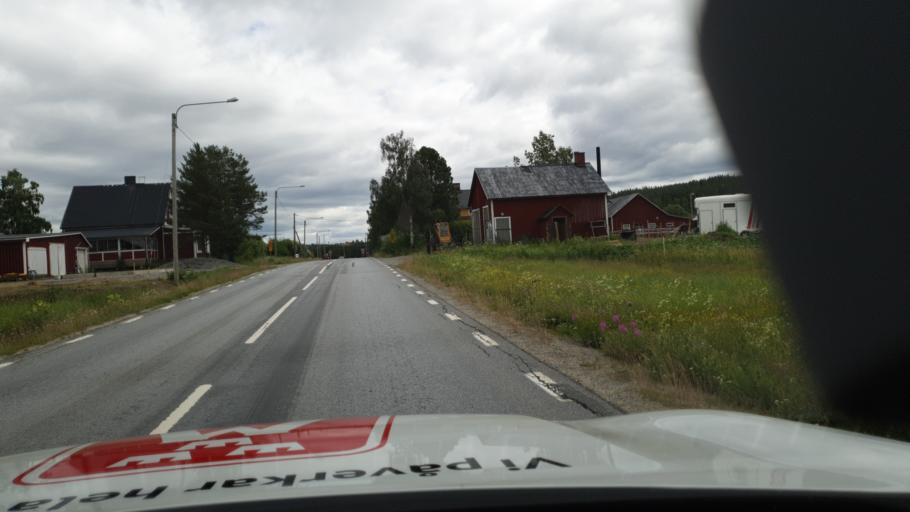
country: SE
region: Vaesterbotten
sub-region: Vannas Kommun
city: Vaennaes
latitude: 63.8990
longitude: 19.6961
